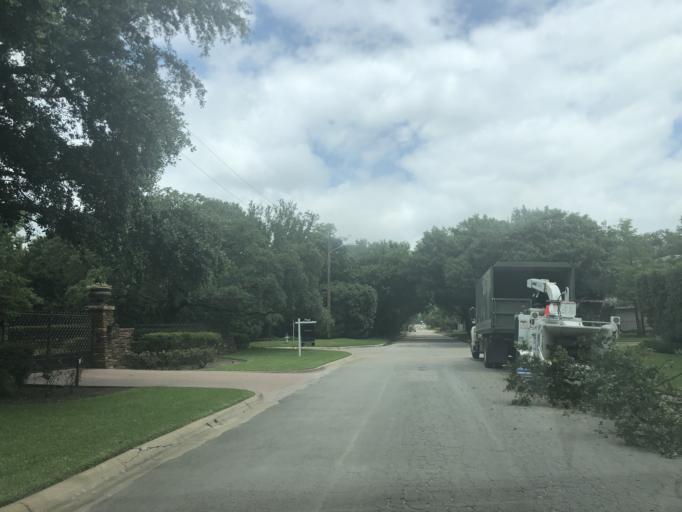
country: US
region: Texas
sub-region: Dallas County
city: University Park
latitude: 32.8894
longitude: -96.8297
